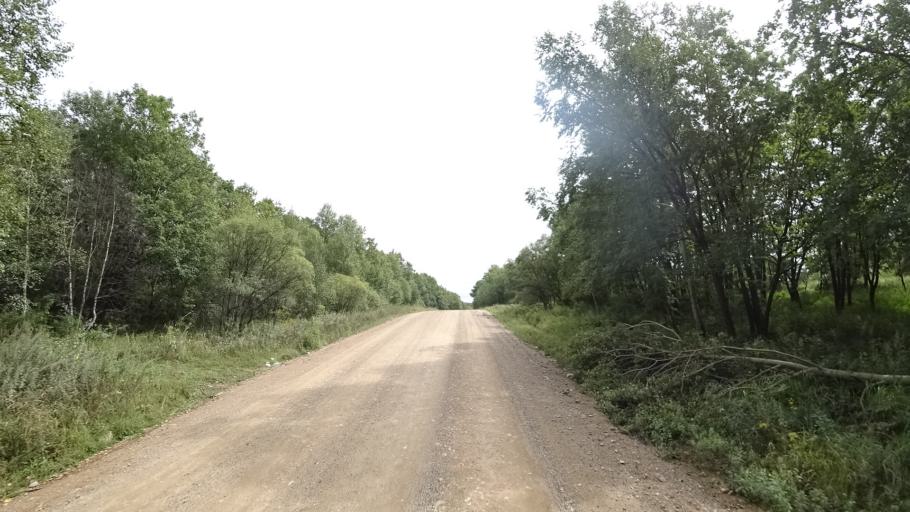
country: RU
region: Primorskiy
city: Lyalichi
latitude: 44.0932
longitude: 132.4328
